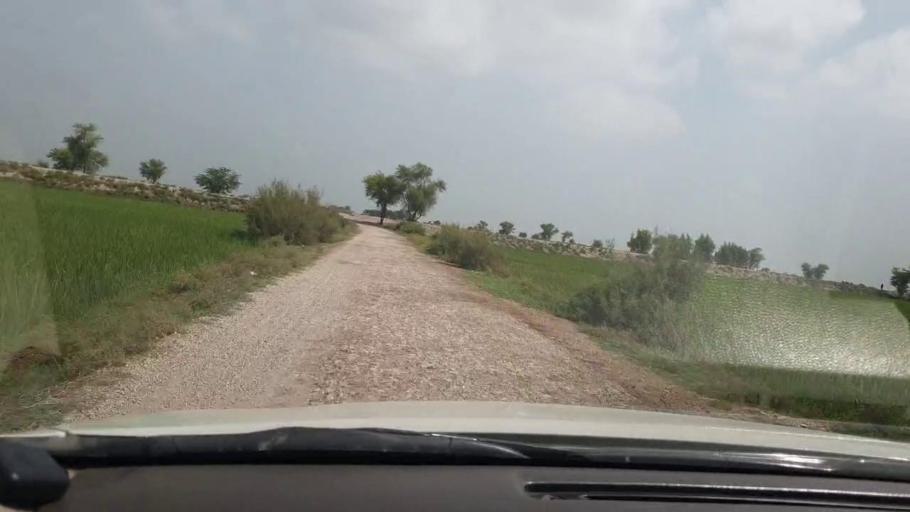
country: PK
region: Sindh
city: Garhi Yasin
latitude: 28.0121
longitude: 68.5403
